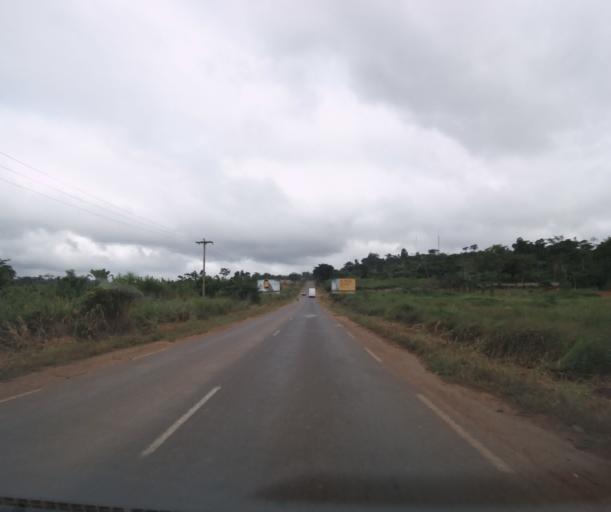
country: CM
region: Centre
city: Mbankomo
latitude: 3.7852
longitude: 11.4546
